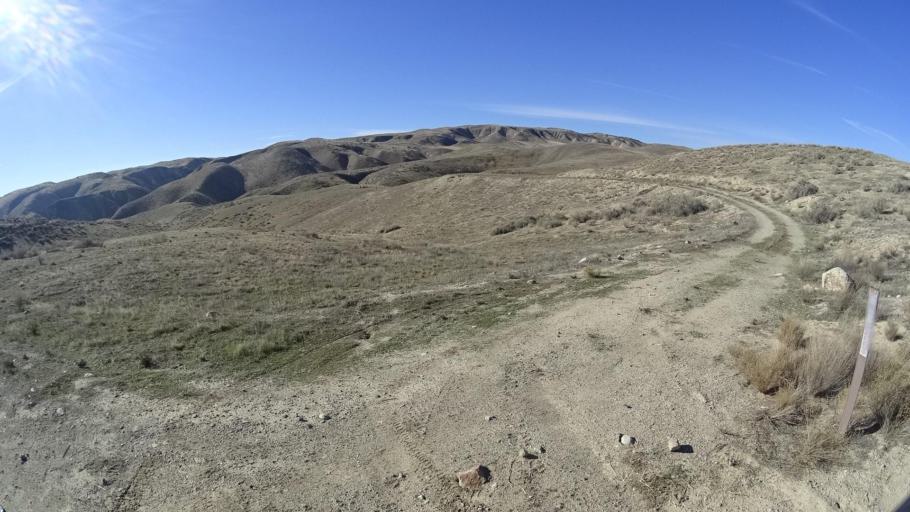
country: US
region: California
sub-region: Kern County
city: Maricopa
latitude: 35.0178
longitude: -119.4728
